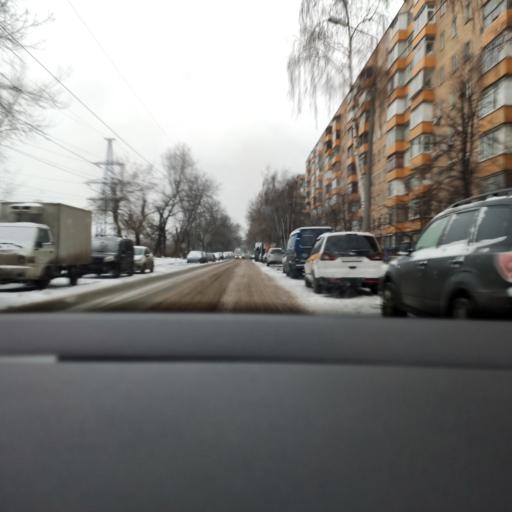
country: RU
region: Moskovskaya
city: Reutov
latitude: 55.7688
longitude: 37.8536
